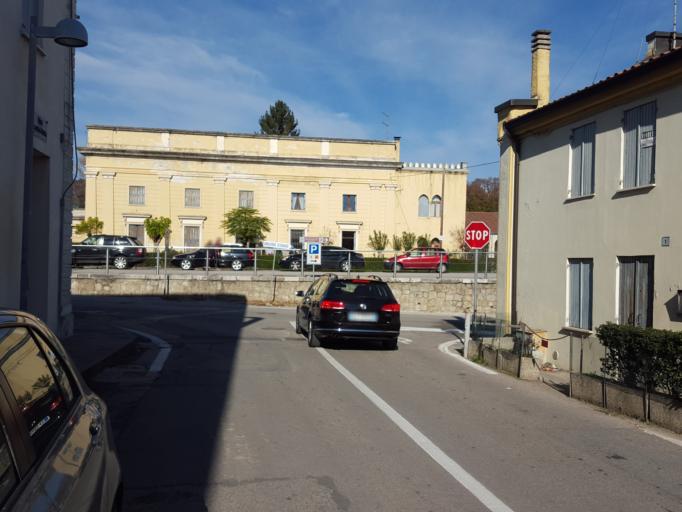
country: IT
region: Veneto
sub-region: Provincia di Padova
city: Piazzola sul Brenta
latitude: 45.5434
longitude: 11.7878
